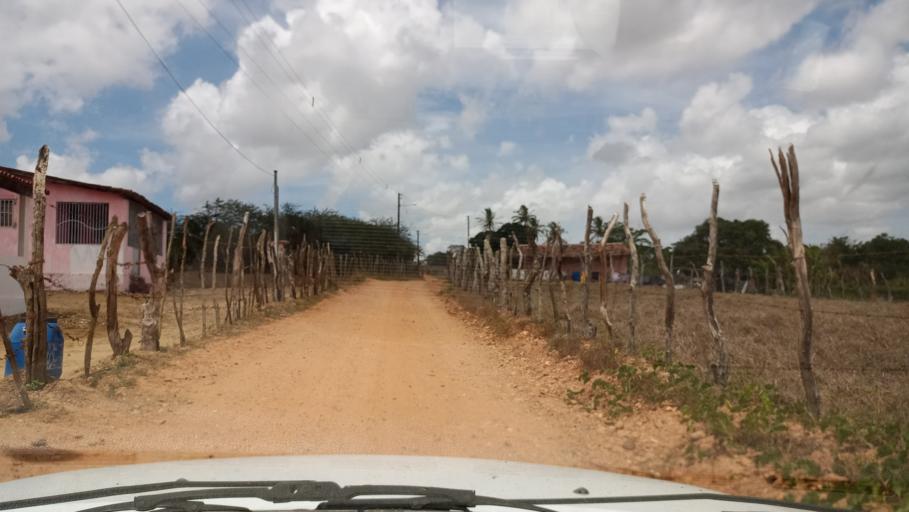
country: BR
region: Rio Grande do Norte
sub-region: Goianinha
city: Goianinha
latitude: -6.2966
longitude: -35.2784
